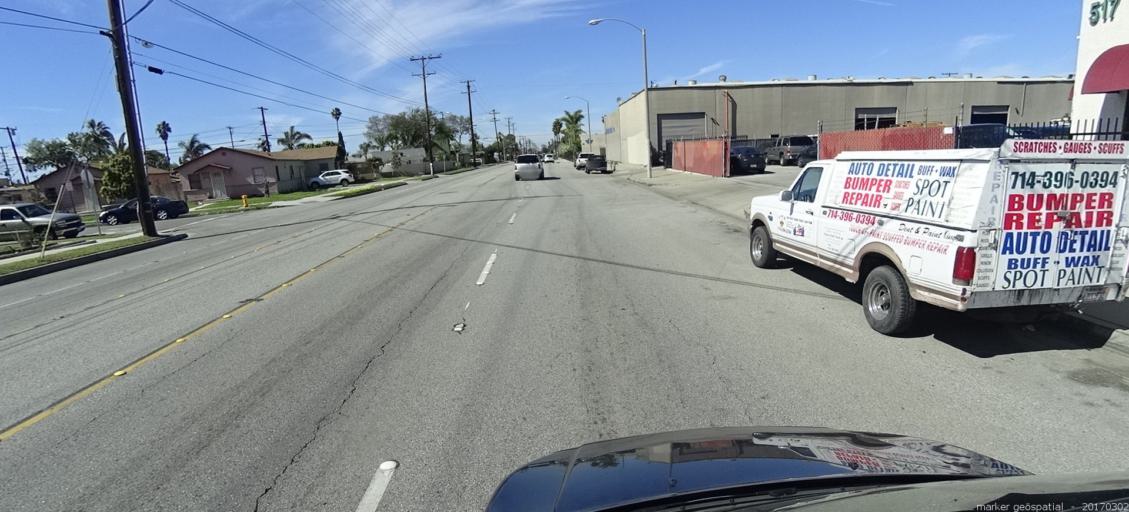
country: US
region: California
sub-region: Orange County
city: Anaheim
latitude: 33.8473
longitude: -117.9113
